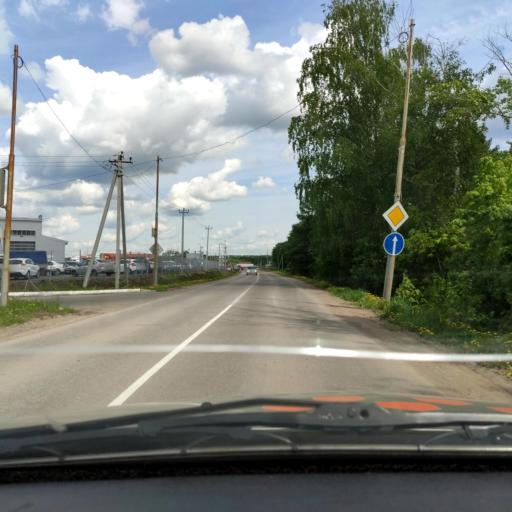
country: RU
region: Bashkortostan
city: Avdon
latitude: 54.6550
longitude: 55.7001
